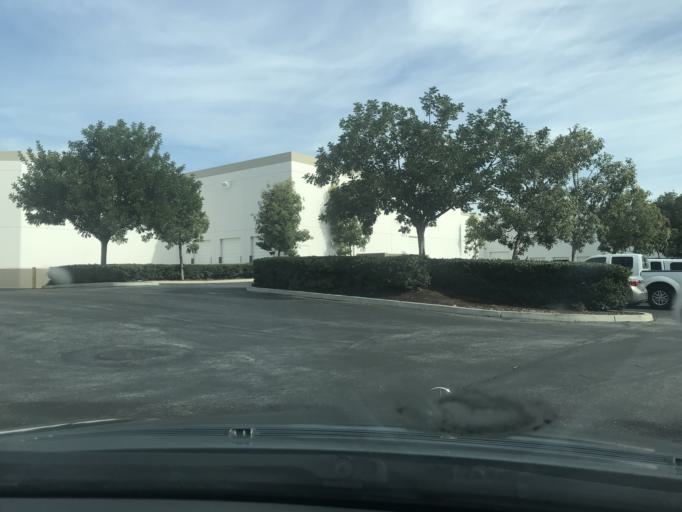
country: US
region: California
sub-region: Los Angeles County
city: Santa Fe Springs
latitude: 33.9326
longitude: -118.0632
